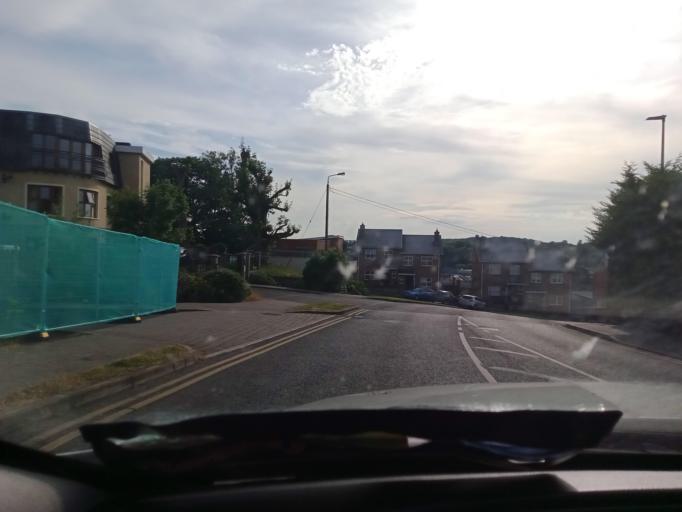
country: IE
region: Ulster
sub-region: An Cabhan
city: Cavan
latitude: 53.9928
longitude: -7.3569
